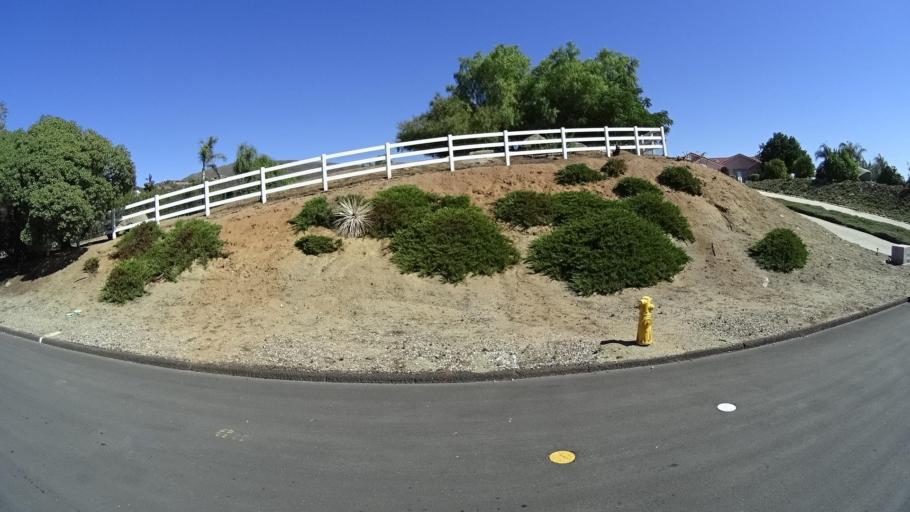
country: US
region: California
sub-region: San Diego County
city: Alpine
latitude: 32.8415
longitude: -116.7617
